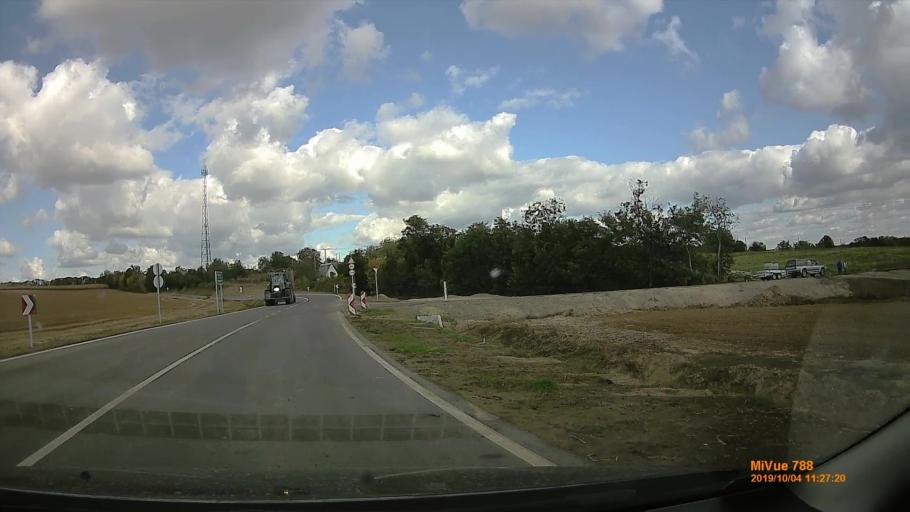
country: HU
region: Somogy
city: Kaposvar
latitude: 46.5152
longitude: 17.8101
